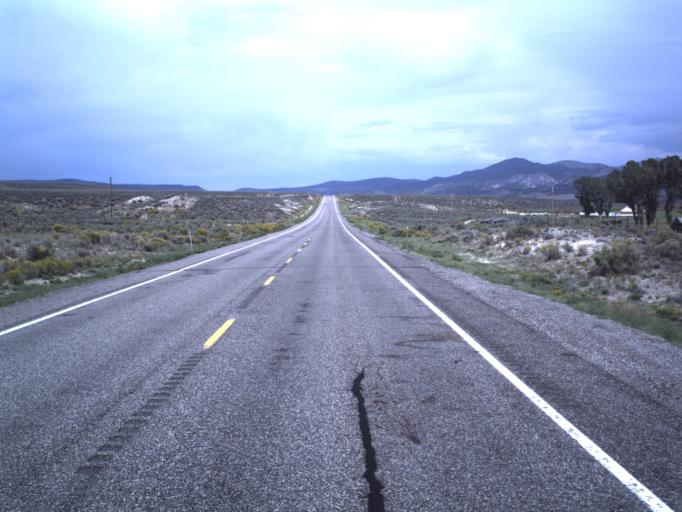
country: US
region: Utah
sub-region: Garfield County
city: Panguitch
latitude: 37.9725
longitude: -112.4076
